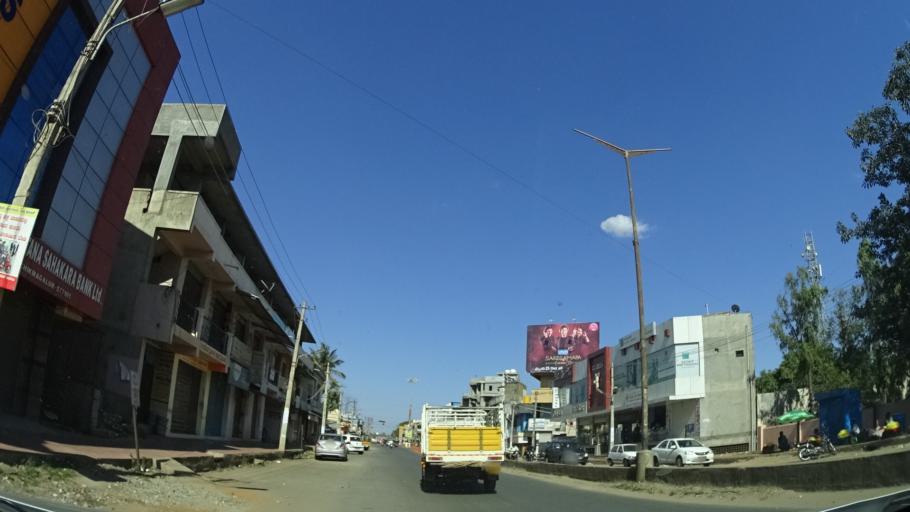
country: IN
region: Karnataka
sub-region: Chikmagalur
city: Chikmagalur
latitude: 13.3251
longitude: 75.7730
